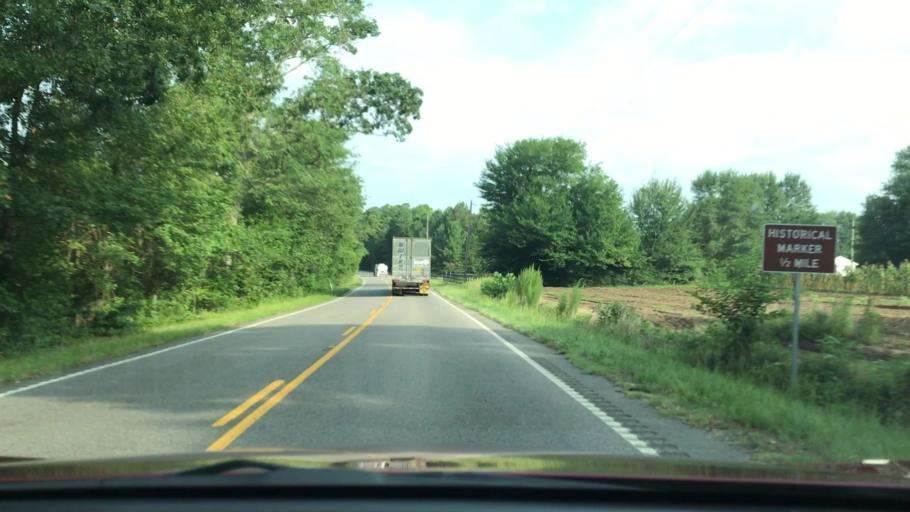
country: US
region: South Carolina
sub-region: Barnwell County
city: Williston
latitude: 33.6191
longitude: -81.2889
